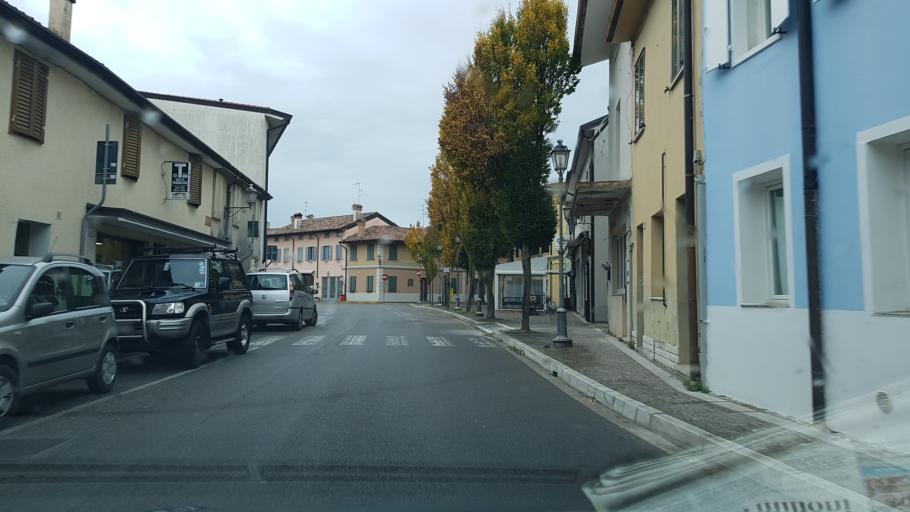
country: IT
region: Friuli Venezia Giulia
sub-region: Provincia di Gorizia
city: San Pier d'Isonzo
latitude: 45.8470
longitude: 13.4599
